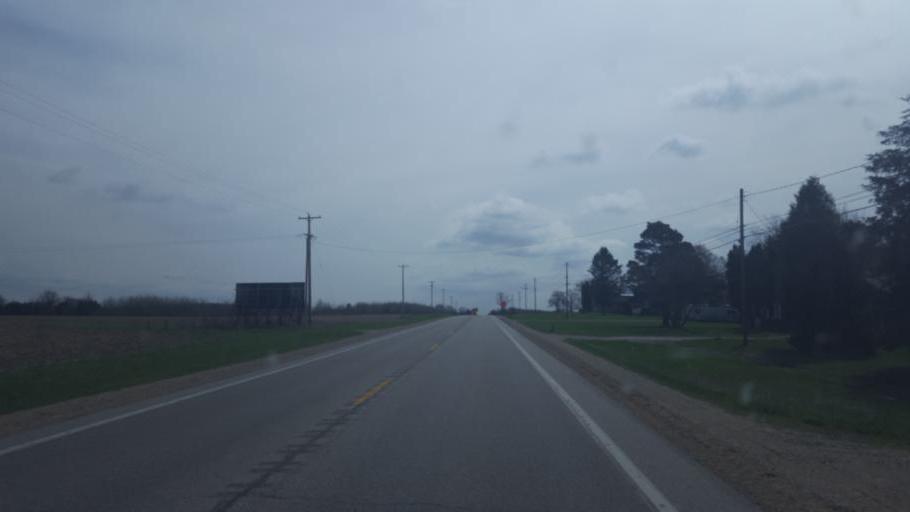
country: US
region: Michigan
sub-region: Montcalm County
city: Edmore
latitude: 43.4080
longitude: -85.0106
